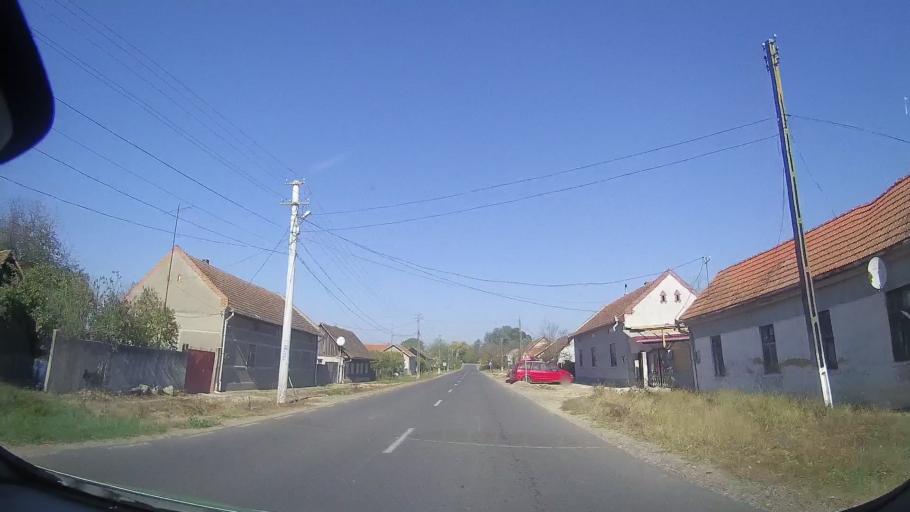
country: RO
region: Timis
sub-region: Comuna Balint
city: Balint
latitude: 45.8092
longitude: 21.8595
